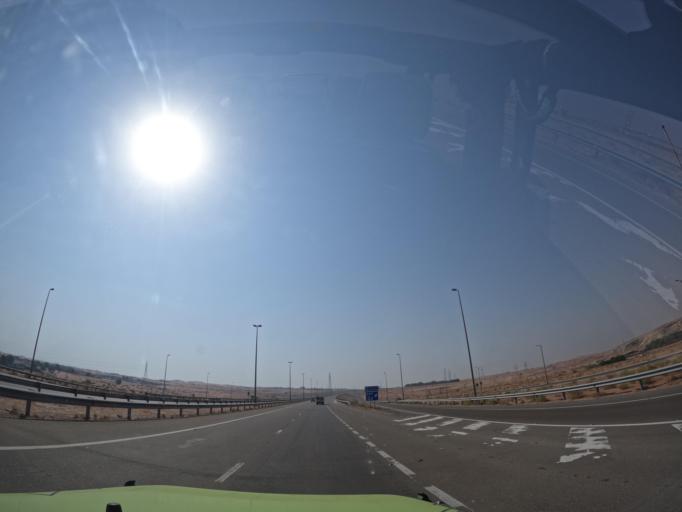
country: OM
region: Al Buraimi
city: Al Buraymi
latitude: 24.3909
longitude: 55.7233
